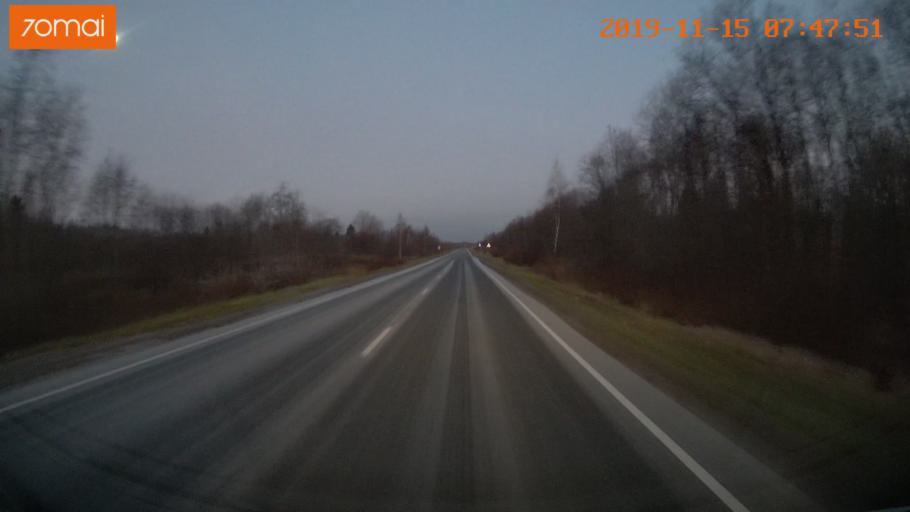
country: RU
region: Vologda
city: Sheksna
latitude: 58.8454
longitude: 38.2535
